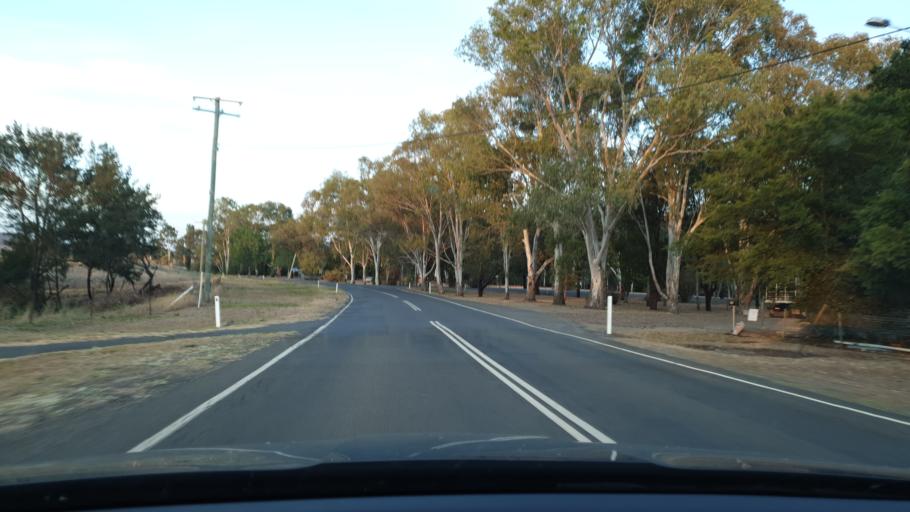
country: AU
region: Queensland
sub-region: Southern Downs
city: Warwick
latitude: -28.0303
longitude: 151.9819
